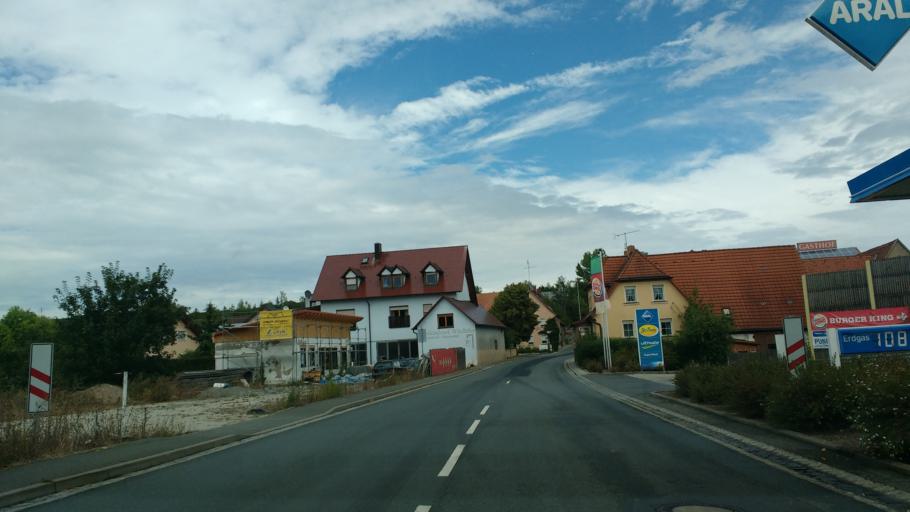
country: DE
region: Bavaria
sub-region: Upper Franconia
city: Schlusselfeld
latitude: 49.7460
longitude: 10.6333
